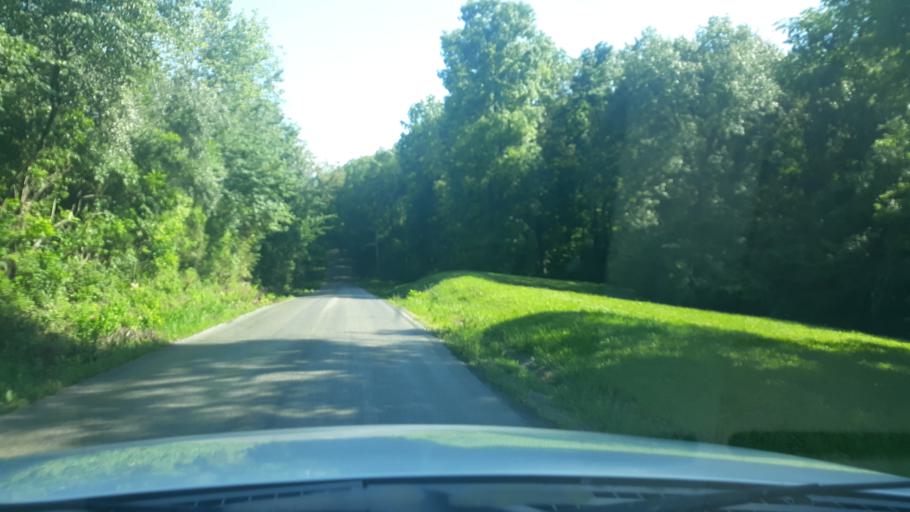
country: US
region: Illinois
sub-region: Saline County
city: Harrisburg
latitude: 37.8468
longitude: -88.5813
